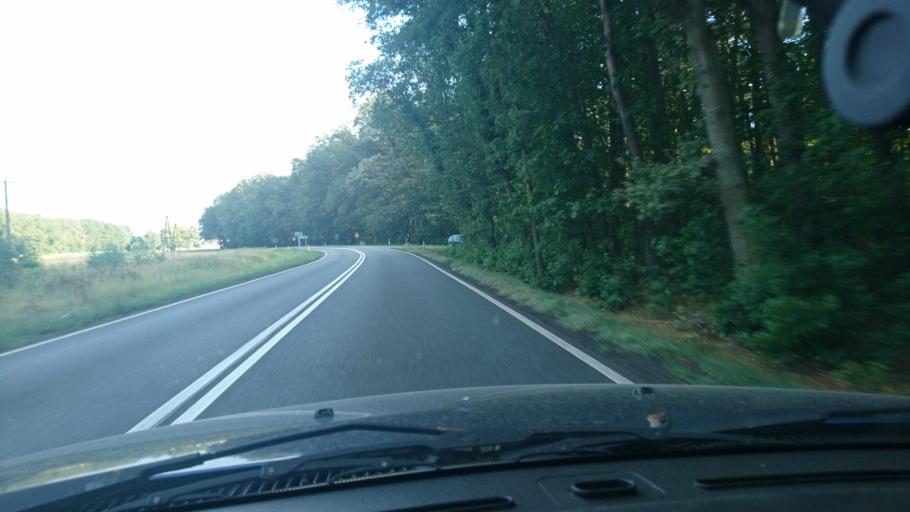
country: PL
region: Opole Voivodeship
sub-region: Powiat oleski
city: Olesno
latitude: 50.9219
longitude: 18.3387
